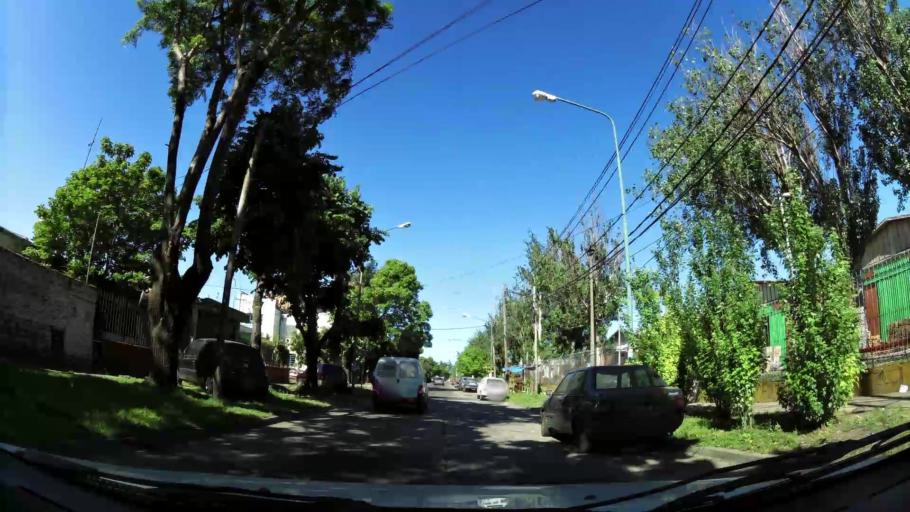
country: AR
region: Buenos Aires
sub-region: Partido de General San Martin
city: General San Martin
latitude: -34.5463
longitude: -58.5232
